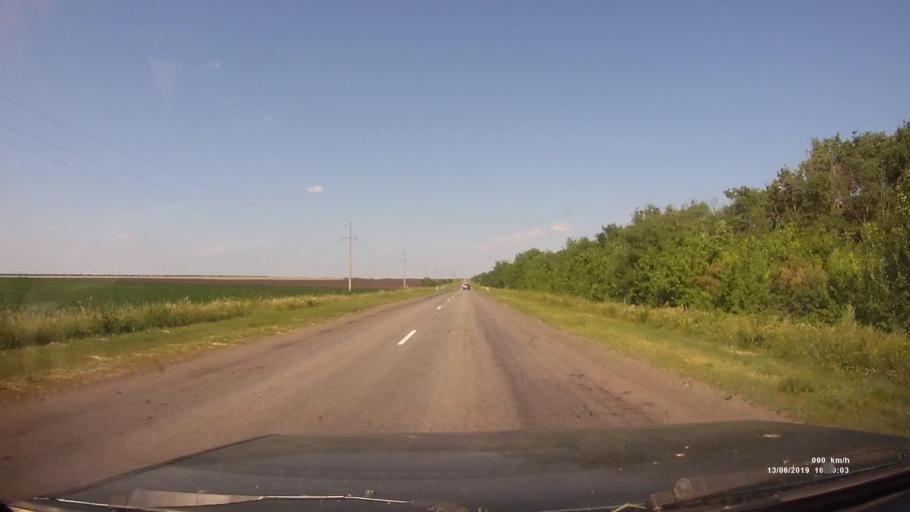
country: RU
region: Rostov
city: Kazanskaya
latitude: 49.8352
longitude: 41.2273
